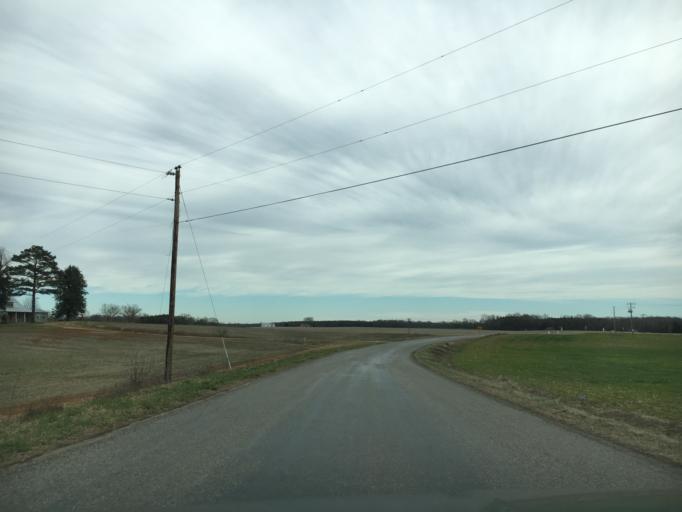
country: US
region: Virginia
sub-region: Amelia County
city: Amelia Court House
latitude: 37.4033
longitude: -77.9709
